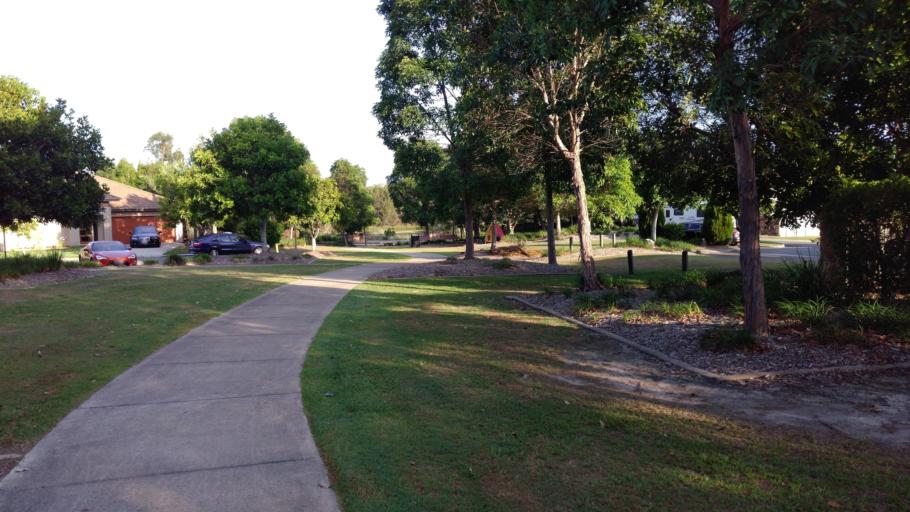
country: AU
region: Queensland
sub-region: Moreton Bay
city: Deception Bay
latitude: -27.2112
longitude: 153.0267
